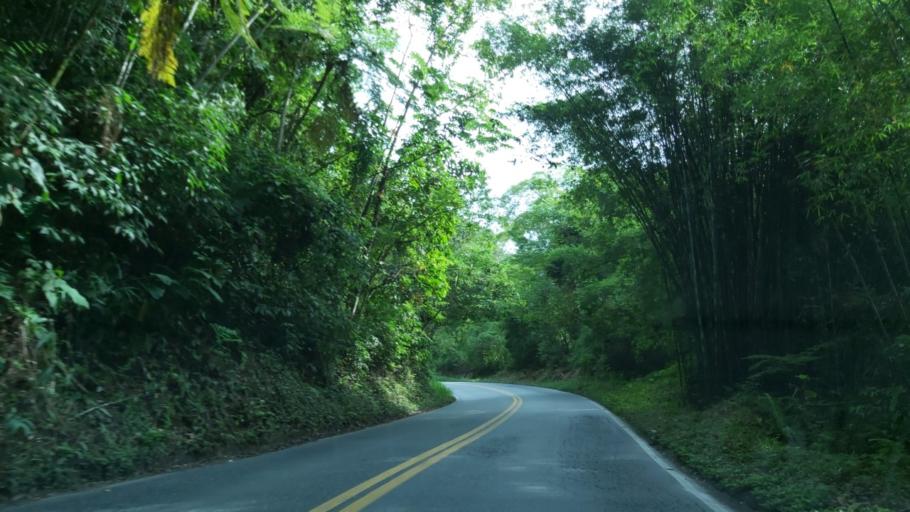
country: BR
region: Sao Paulo
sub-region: Juquia
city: Juquia
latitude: -24.1092
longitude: -47.6265
